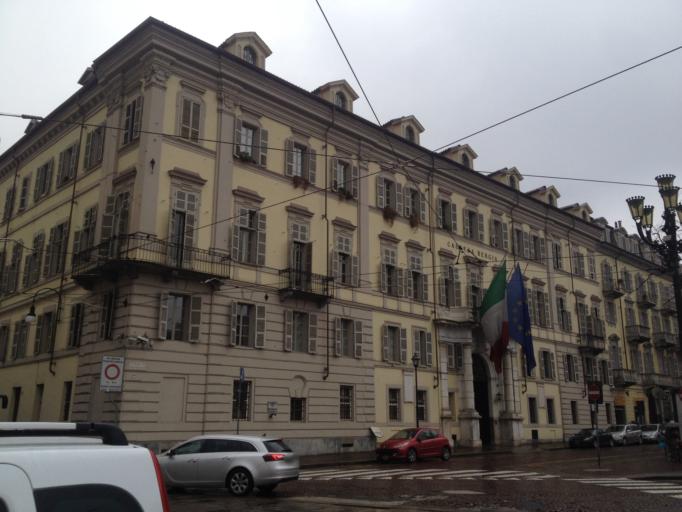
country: IT
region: Piedmont
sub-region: Provincia di Torino
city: Turin
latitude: 45.0660
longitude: 7.6887
